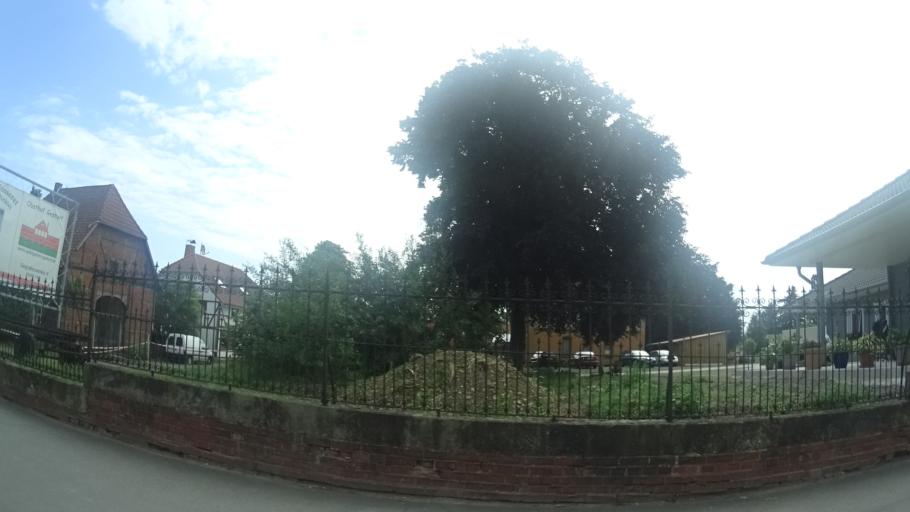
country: DE
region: Lower Saxony
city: Pattensen
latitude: 52.2140
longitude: 9.6998
